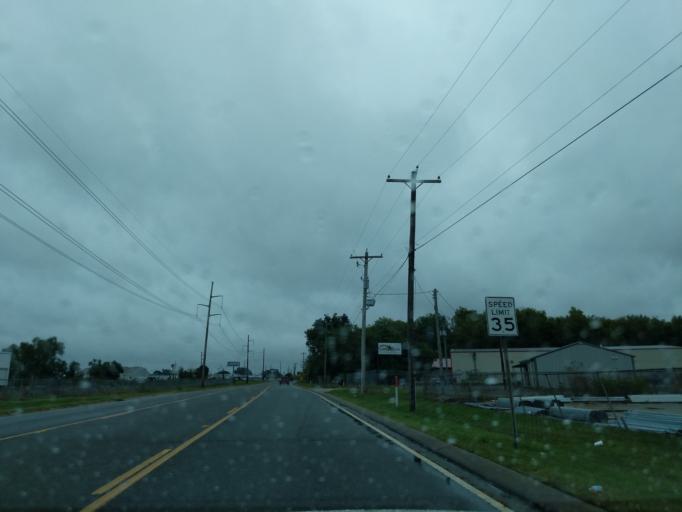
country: US
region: Louisiana
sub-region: Bossier Parish
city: Bossier City
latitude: 32.5249
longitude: -93.6830
